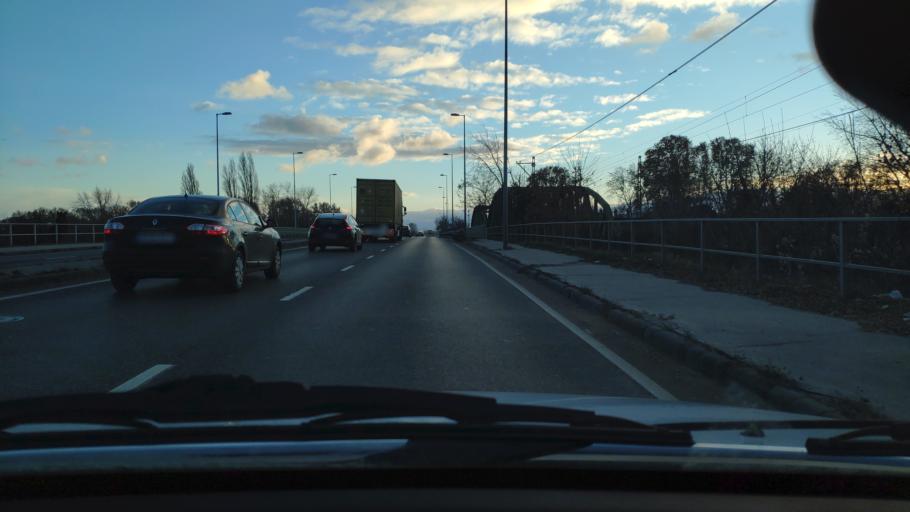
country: HU
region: Budapest
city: Budapest IX. keruelet
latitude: 47.4624
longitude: 19.0725
